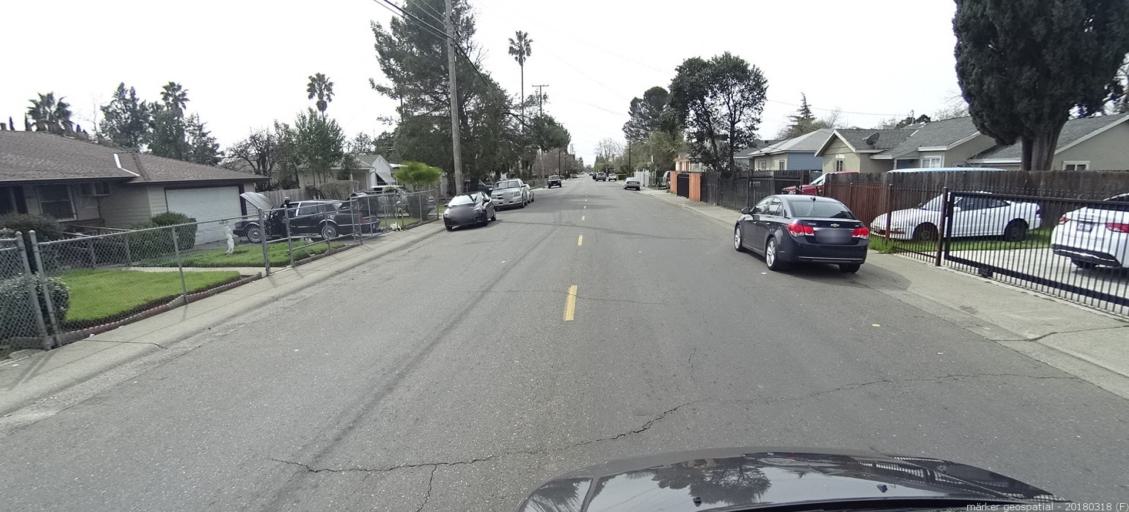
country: US
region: California
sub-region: Sacramento County
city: Parkway
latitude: 38.5320
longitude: -121.4563
